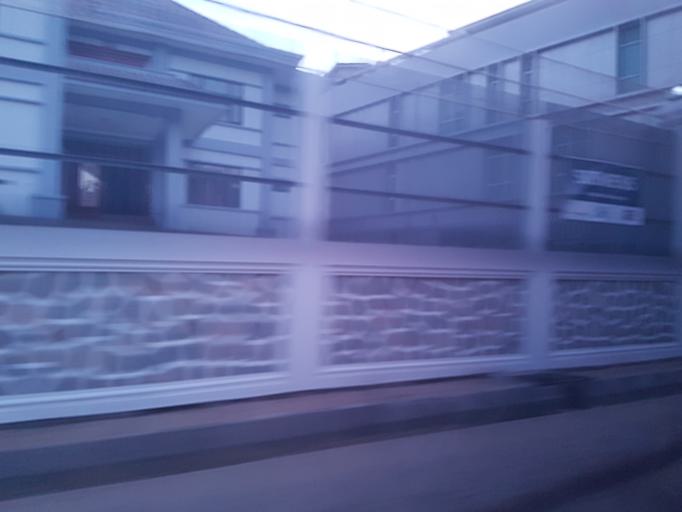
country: MM
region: Yangon
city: Yangon
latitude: 16.8042
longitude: 96.1611
